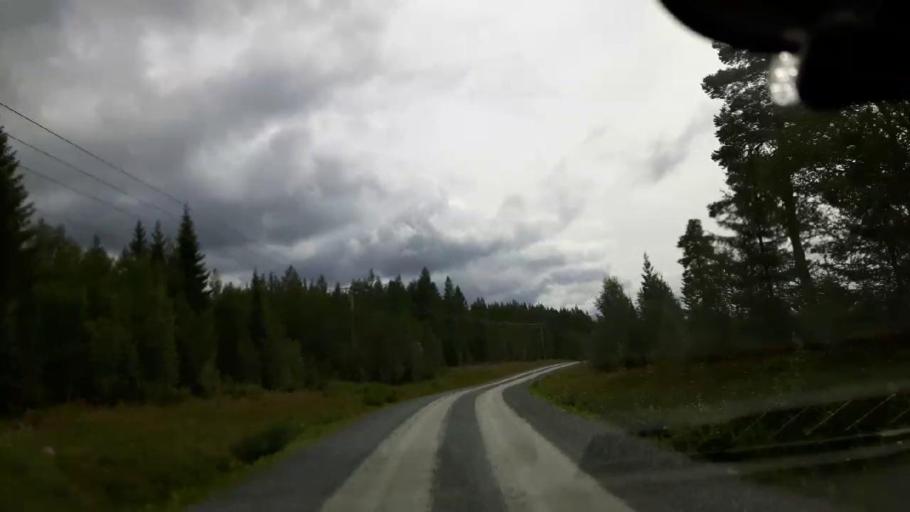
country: SE
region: Jaemtland
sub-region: Krokoms Kommun
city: Valla
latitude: 63.6019
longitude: 14.1347
